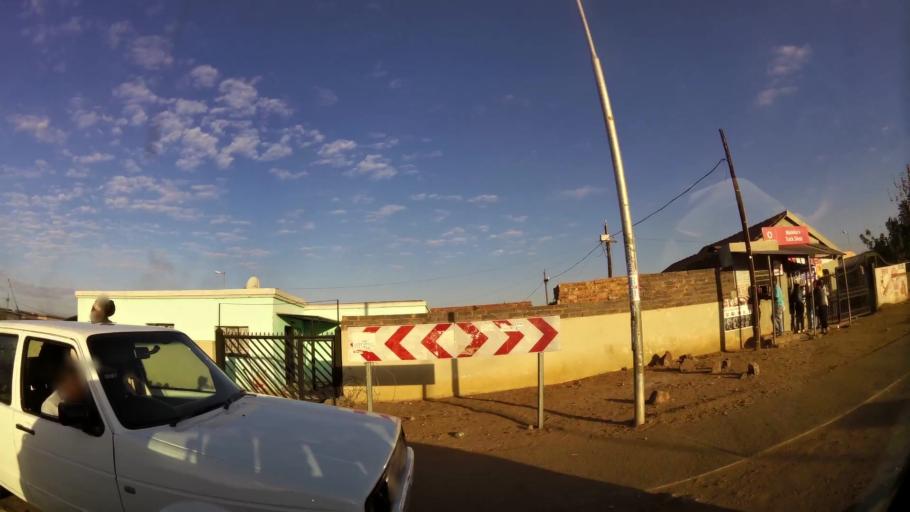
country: ZA
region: Gauteng
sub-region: City of Tshwane Metropolitan Municipality
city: Cullinan
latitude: -25.7118
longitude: 28.3584
